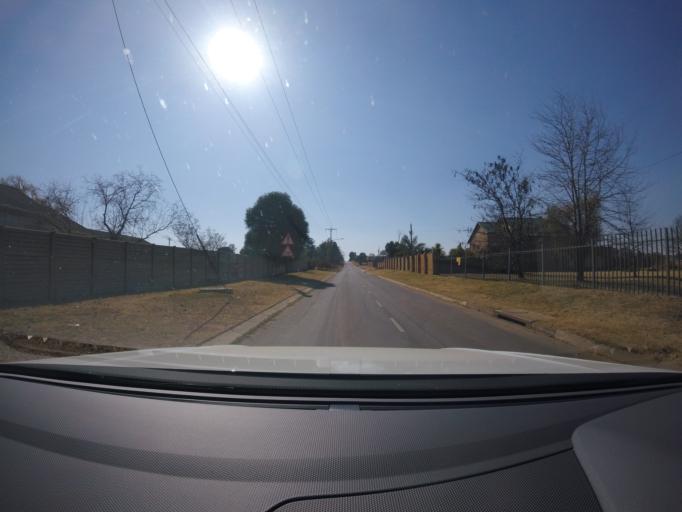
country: ZA
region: Gauteng
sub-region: Ekurhuleni Metropolitan Municipality
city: Benoni
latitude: -26.1235
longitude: 28.3002
